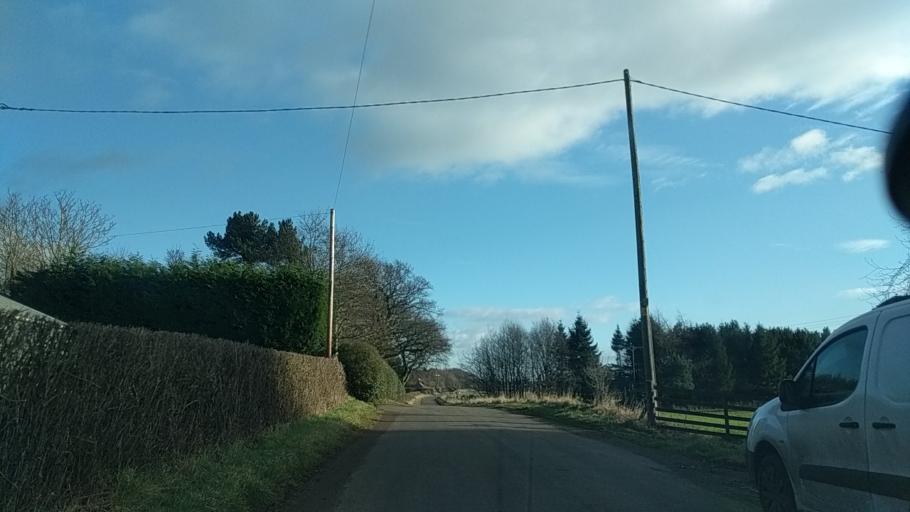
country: GB
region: Scotland
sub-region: West Lothian
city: Broxburn
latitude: 55.9769
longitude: -3.4735
